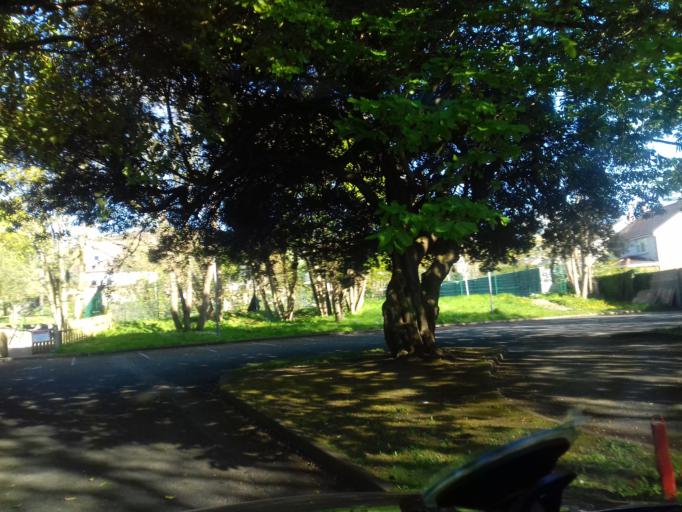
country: IE
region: Leinster
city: Sutton
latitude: 53.3759
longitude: -6.0943
